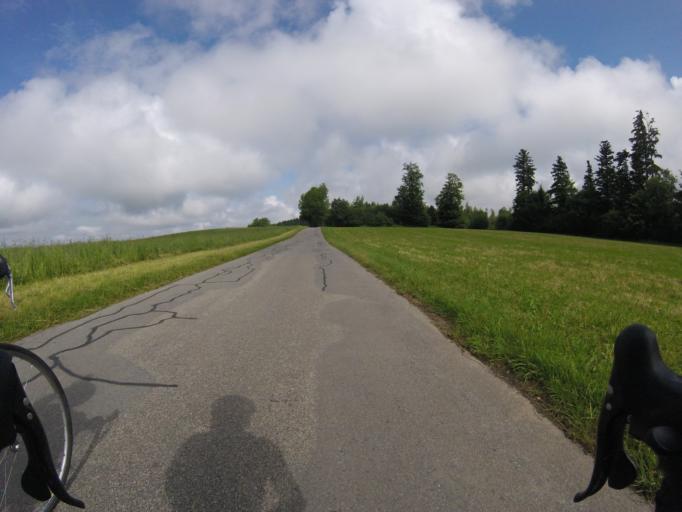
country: CH
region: Bern
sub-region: Bern-Mittelland District
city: Walkringen
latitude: 46.9587
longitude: 7.6009
